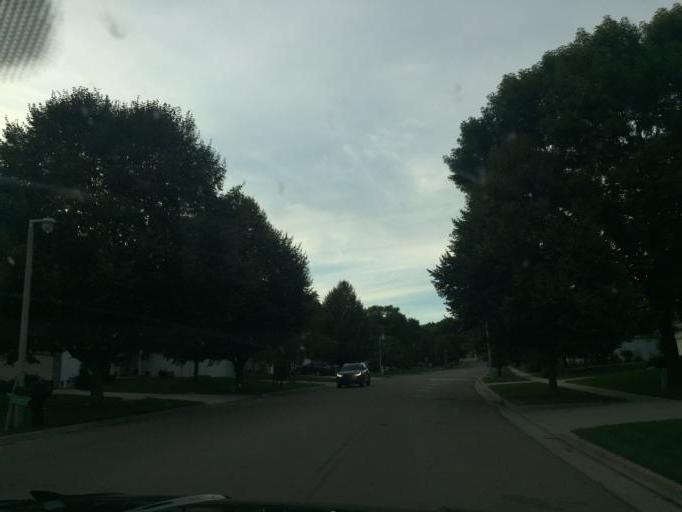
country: US
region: Minnesota
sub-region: Olmsted County
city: Rochester
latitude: 44.0072
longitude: -92.4915
